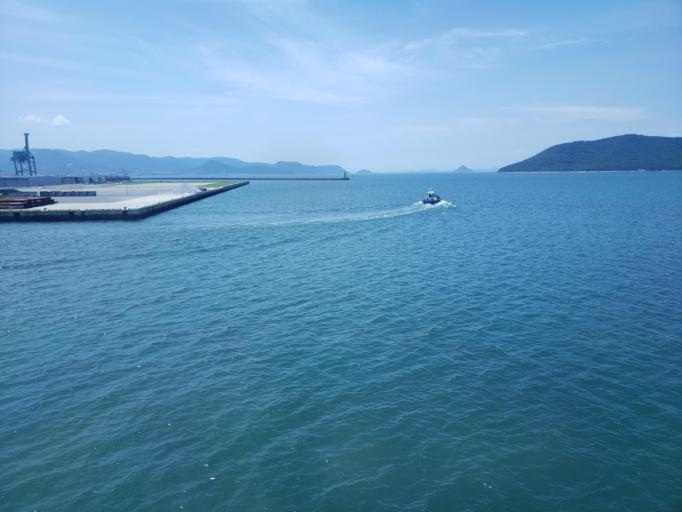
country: JP
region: Kagawa
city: Takamatsu-shi
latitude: 34.3649
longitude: 134.0728
